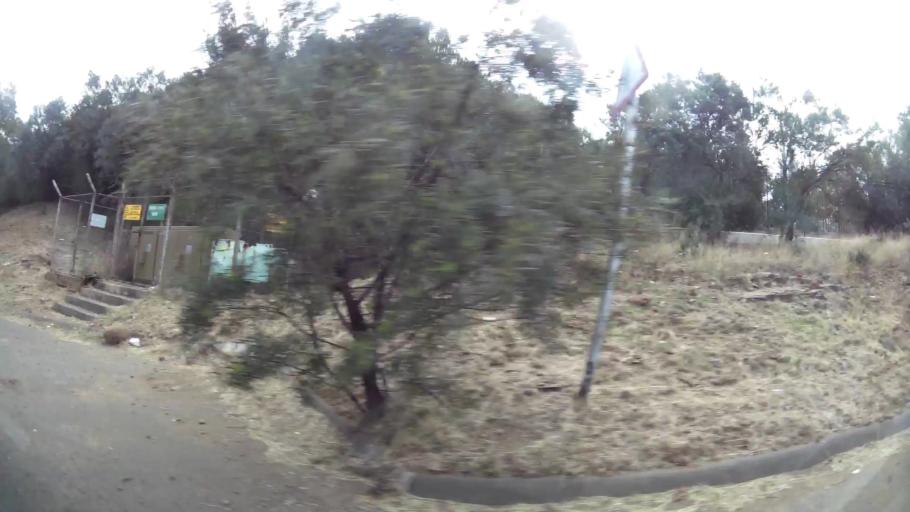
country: ZA
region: Orange Free State
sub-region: Mangaung Metropolitan Municipality
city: Bloemfontein
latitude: -29.1008
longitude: 26.2171
